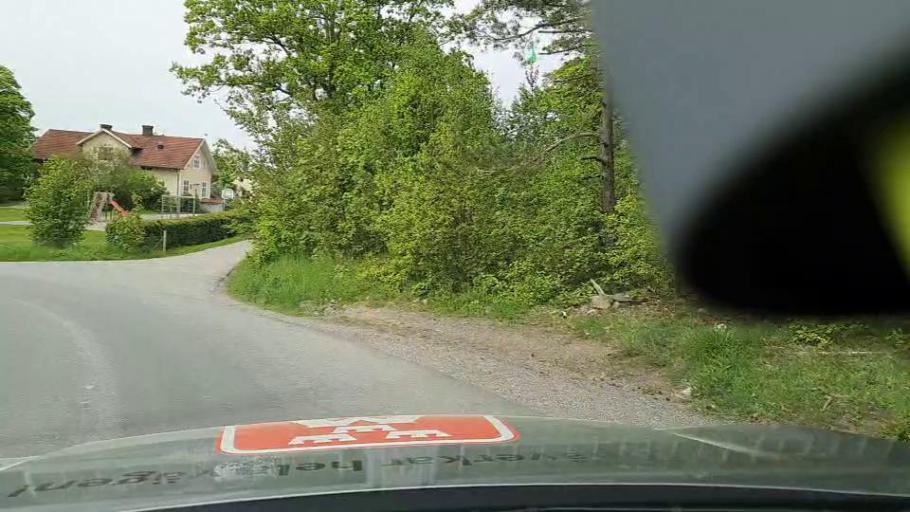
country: SE
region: Soedermanland
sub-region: Flens Kommun
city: Flen
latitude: 59.1015
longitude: 16.5545
